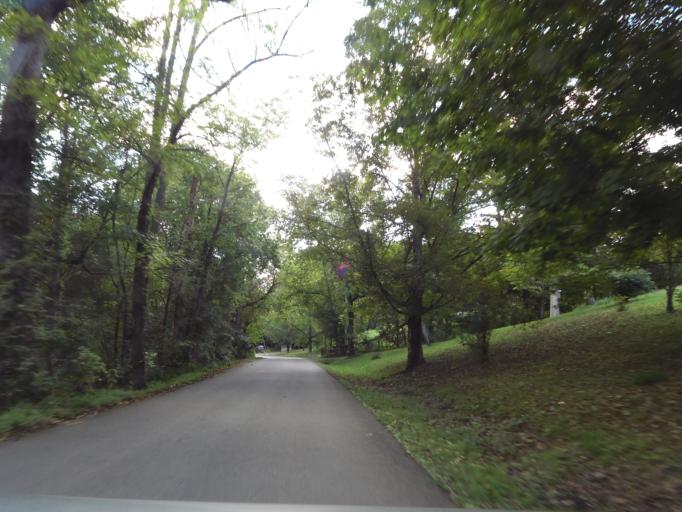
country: US
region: Tennessee
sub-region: Knox County
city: Mascot
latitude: 36.0979
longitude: -83.7712
